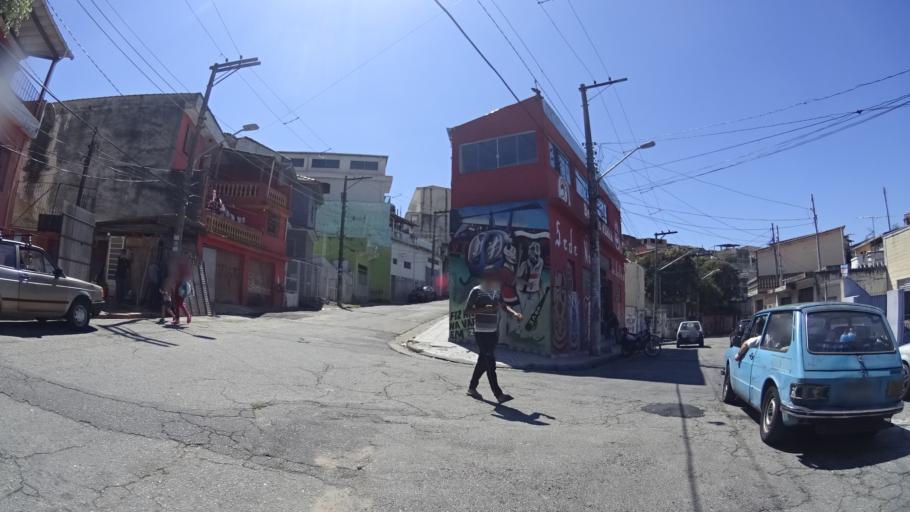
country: BR
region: Sao Paulo
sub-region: Sao Paulo
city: Sao Paulo
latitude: -23.4922
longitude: -46.6658
